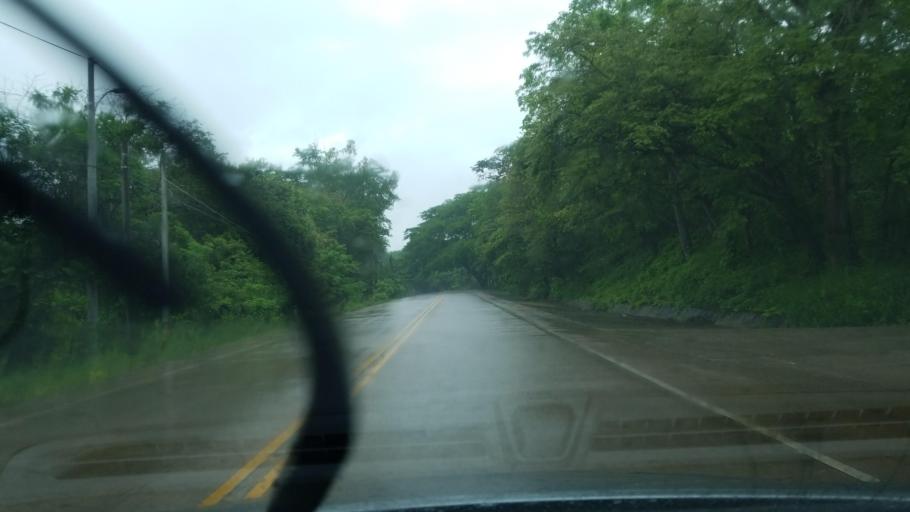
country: HN
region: Copan
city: Copan
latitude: 14.8440
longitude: -89.1406
